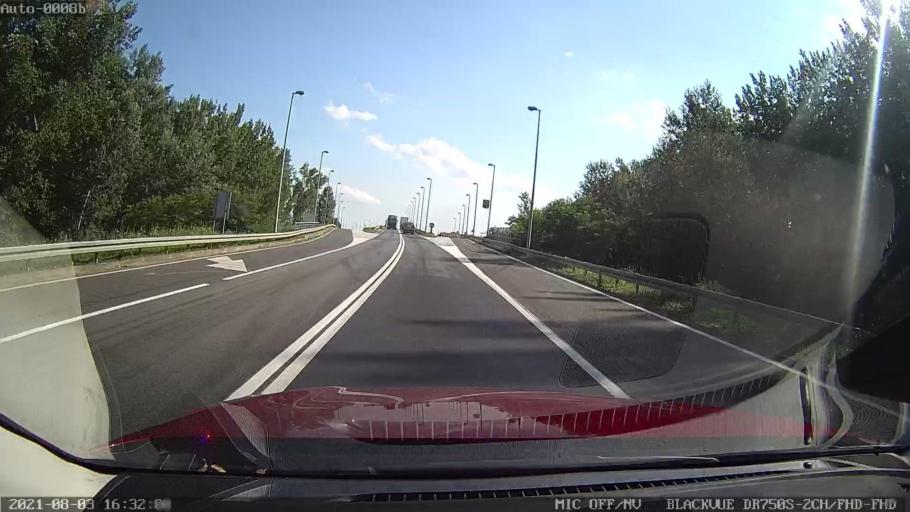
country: HR
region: Osjecko-Baranjska
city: Visnjevac
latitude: 45.5675
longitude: 18.6312
